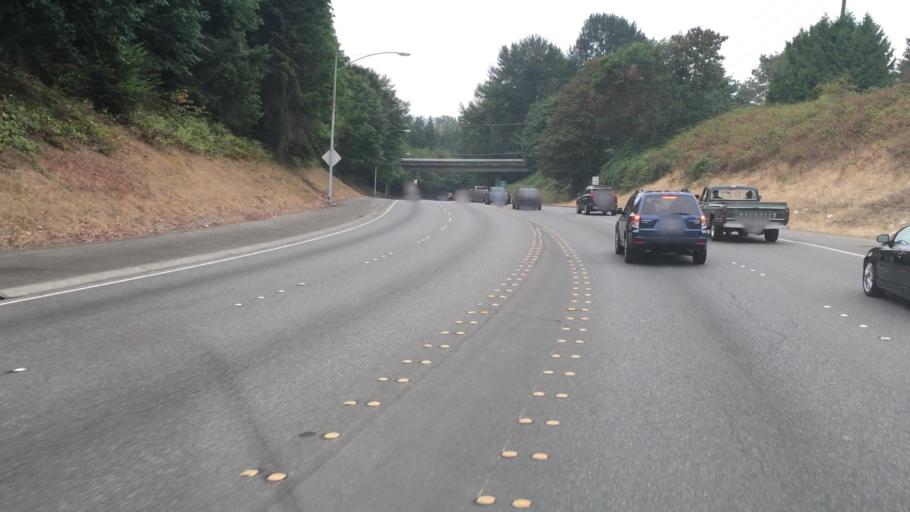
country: US
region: Washington
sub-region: King County
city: Renton
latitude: 47.5020
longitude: -122.1883
